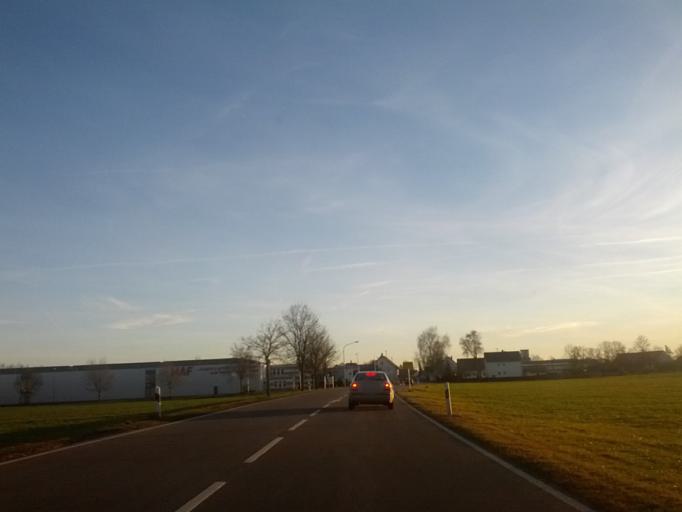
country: DE
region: Bavaria
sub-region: Swabia
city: Fellheim
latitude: 48.0794
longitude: 10.1505
